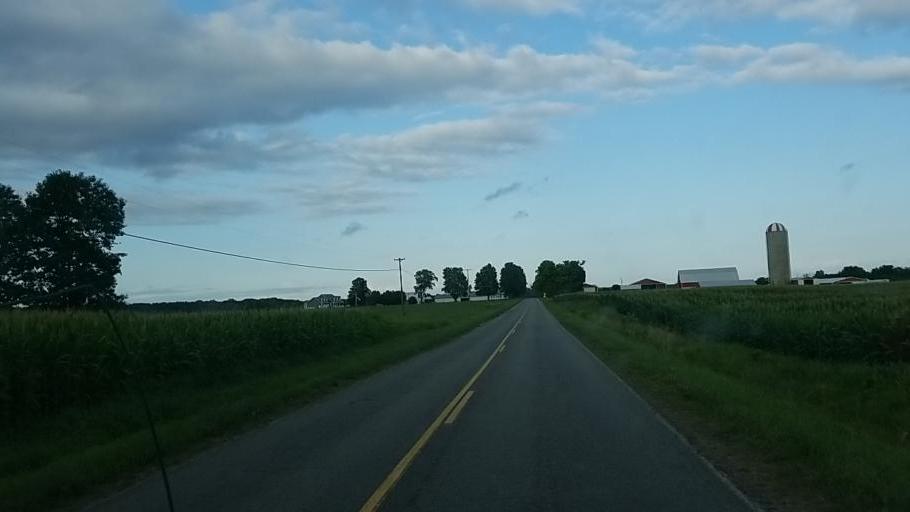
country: US
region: Michigan
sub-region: Montcalm County
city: Howard City
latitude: 43.3374
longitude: -85.3494
